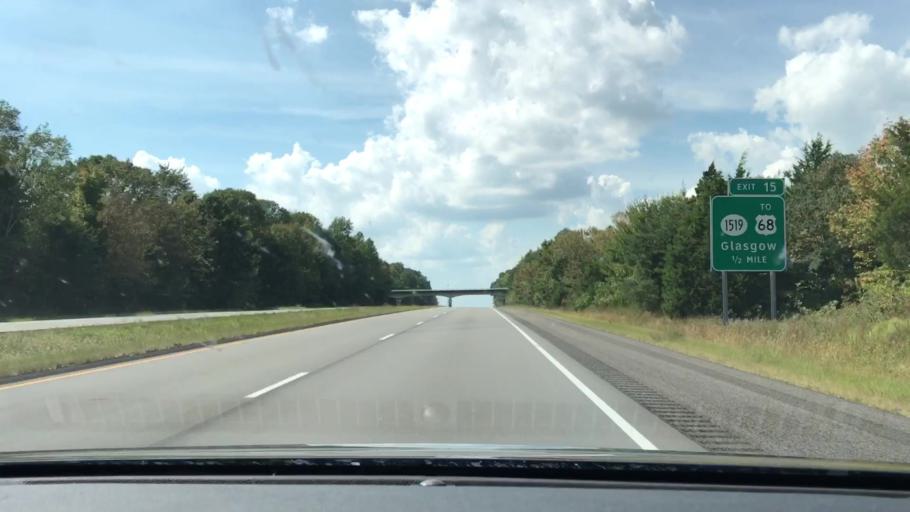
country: US
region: Kentucky
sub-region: Barren County
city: Glasgow
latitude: 36.9964
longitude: -85.8596
